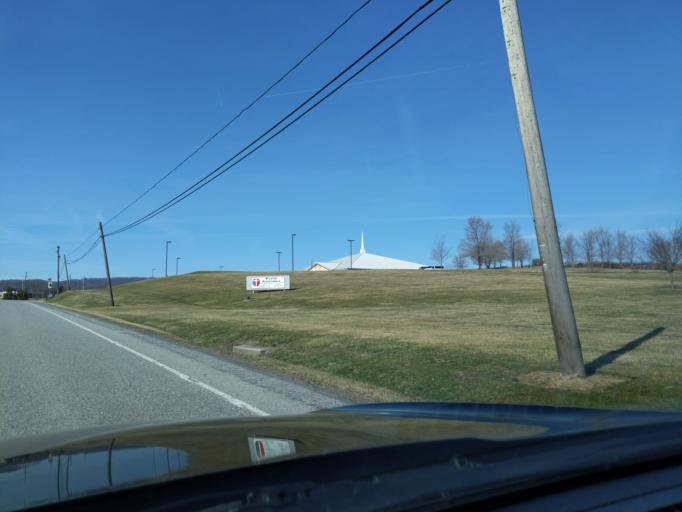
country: US
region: Pennsylvania
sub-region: Blair County
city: Roaring Spring
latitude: 40.3348
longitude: -78.3791
